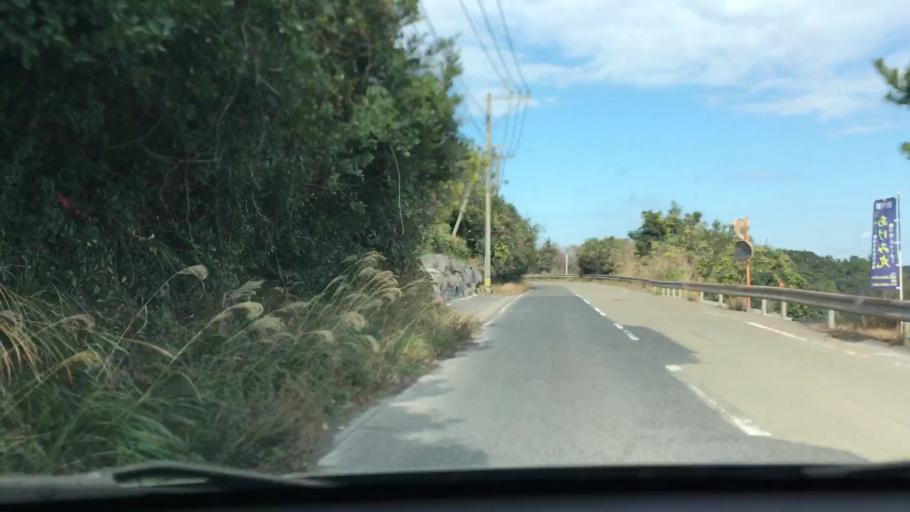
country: JP
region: Kagoshima
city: Hamanoichi
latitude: 31.6170
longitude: 130.6998
